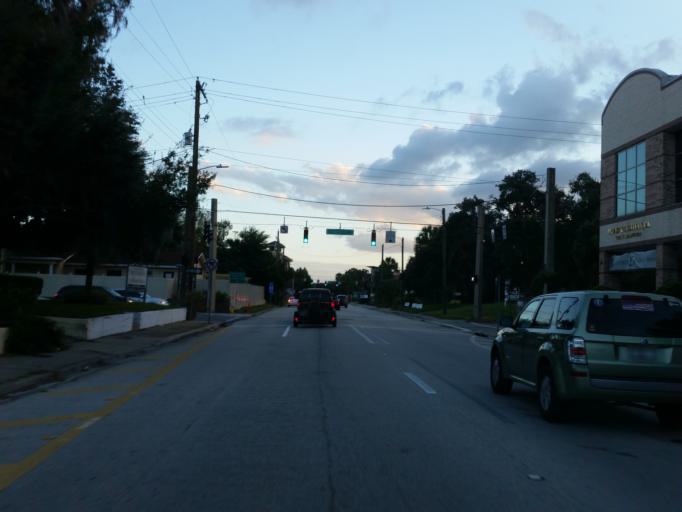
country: US
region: Florida
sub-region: Hillsborough County
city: Tampa
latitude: 27.9438
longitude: -82.4851
